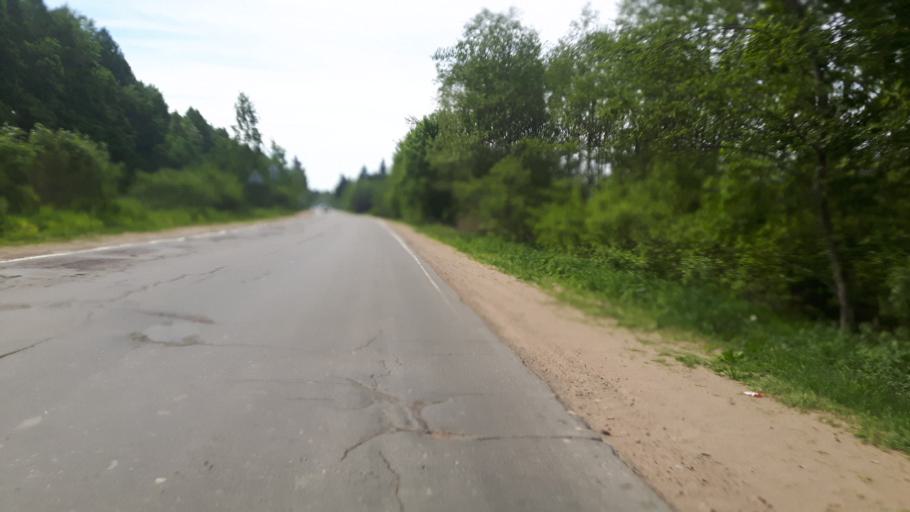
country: RU
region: Leningrad
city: Ust'-Luga
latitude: 59.6412
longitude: 28.2906
